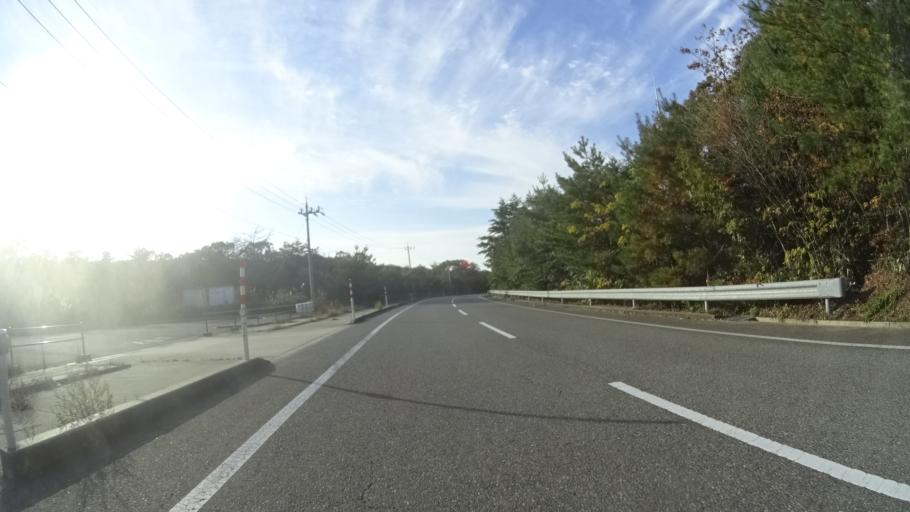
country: JP
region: Ishikawa
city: Hakui
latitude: 37.0711
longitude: 136.7380
